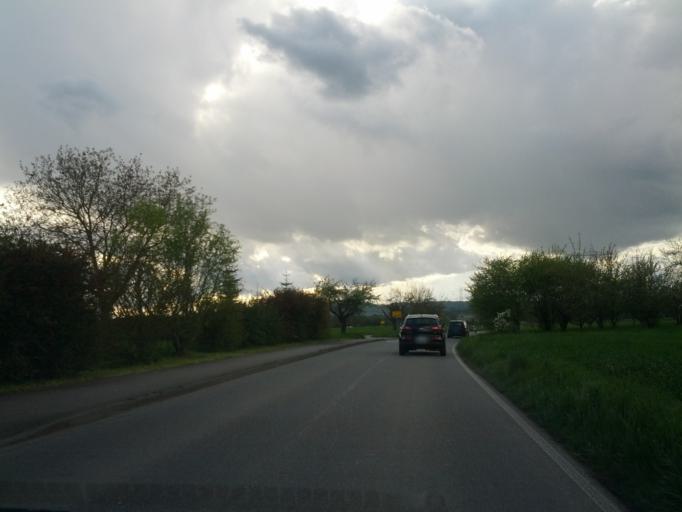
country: DE
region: Baden-Wuerttemberg
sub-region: Freiburg Region
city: Vorstetten
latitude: 48.0754
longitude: 7.8197
